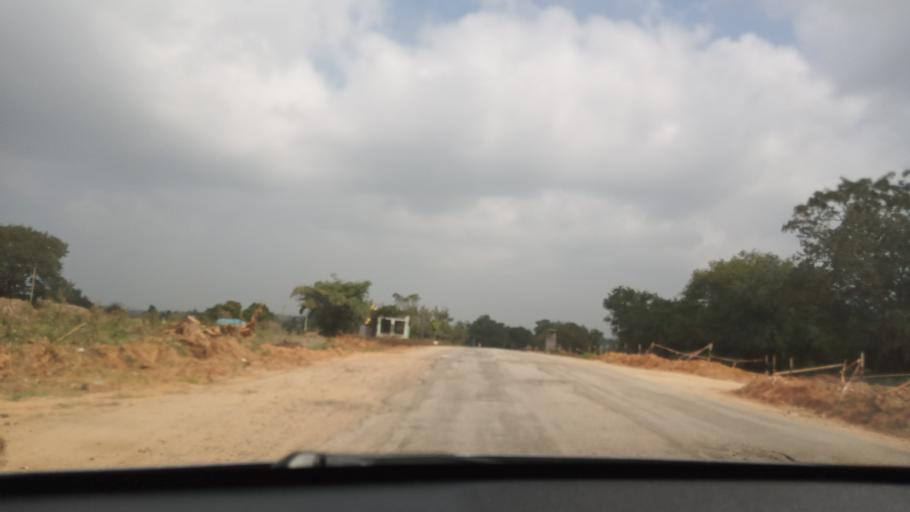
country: IN
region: Karnataka
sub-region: Kolar
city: Srinivaspur
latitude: 13.4428
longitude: 78.2328
